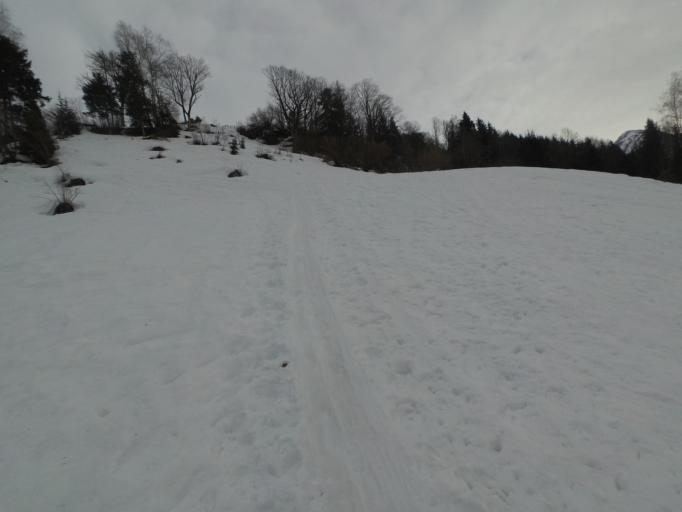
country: AT
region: Salzburg
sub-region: Politischer Bezirk Sankt Johann im Pongau
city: Sankt Johann im Pongau
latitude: 47.3283
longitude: 13.2100
